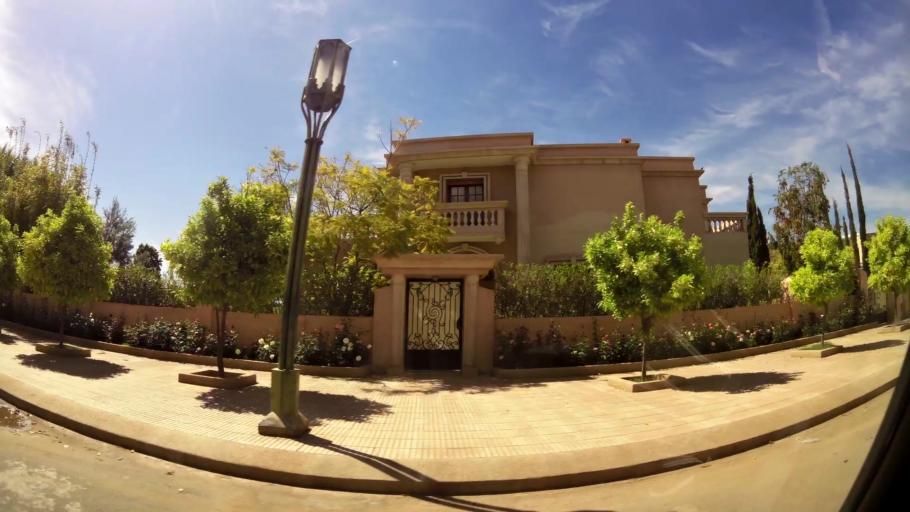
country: MA
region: Marrakech-Tensift-Al Haouz
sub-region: Marrakech
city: Marrakesh
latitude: 31.6187
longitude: -7.9238
